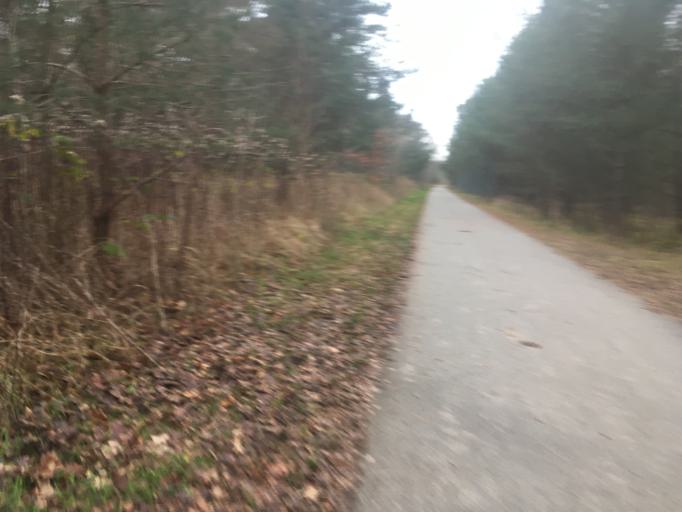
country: DE
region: Mecklenburg-Vorpommern
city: Sagard
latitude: 54.4591
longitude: 13.5669
